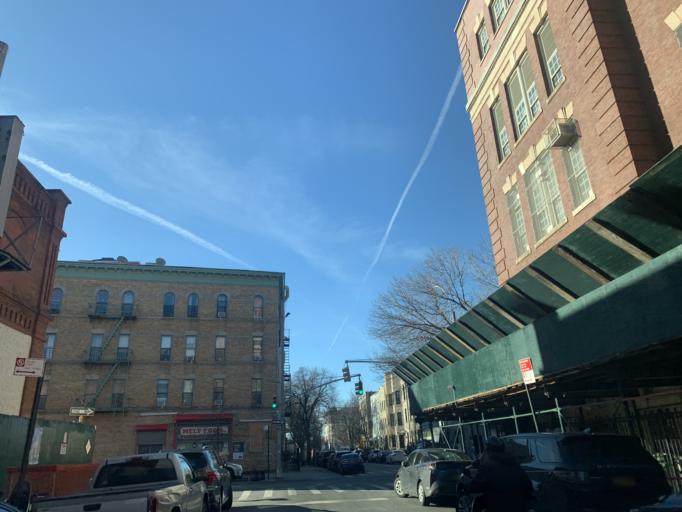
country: US
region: New York
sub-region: Kings County
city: East New York
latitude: 40.6931
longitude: -73.9209
